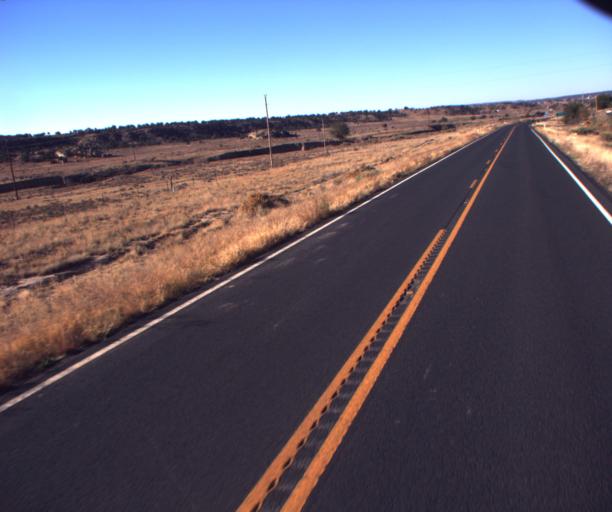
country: US
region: Arizona
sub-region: Apache County
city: Ganado
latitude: 35.7481
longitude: -109.8503
